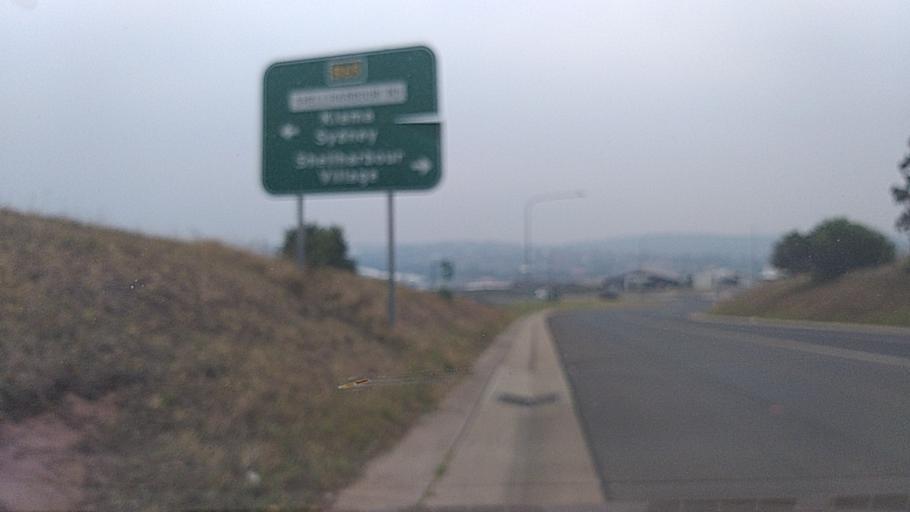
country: AU
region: New South Wales
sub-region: Shellharbour
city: Croom
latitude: -34.5909
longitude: 150.8484
